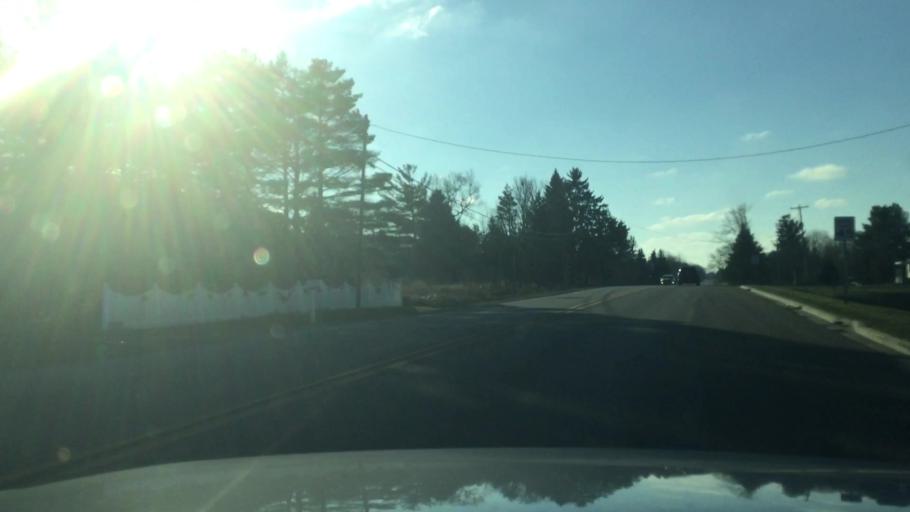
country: US
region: Michigan
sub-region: Genesee County
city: Grand Blanc
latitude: 42.9431
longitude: -83.6625
